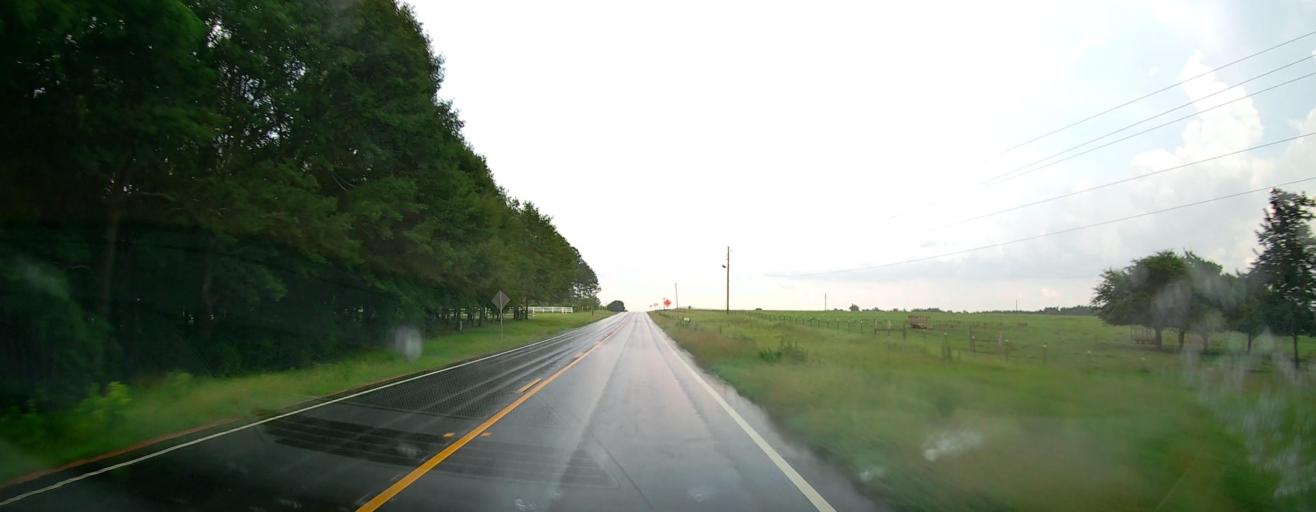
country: US
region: Georgia
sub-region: Dodge County
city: Chester
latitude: 32.5533
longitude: -83.1417
